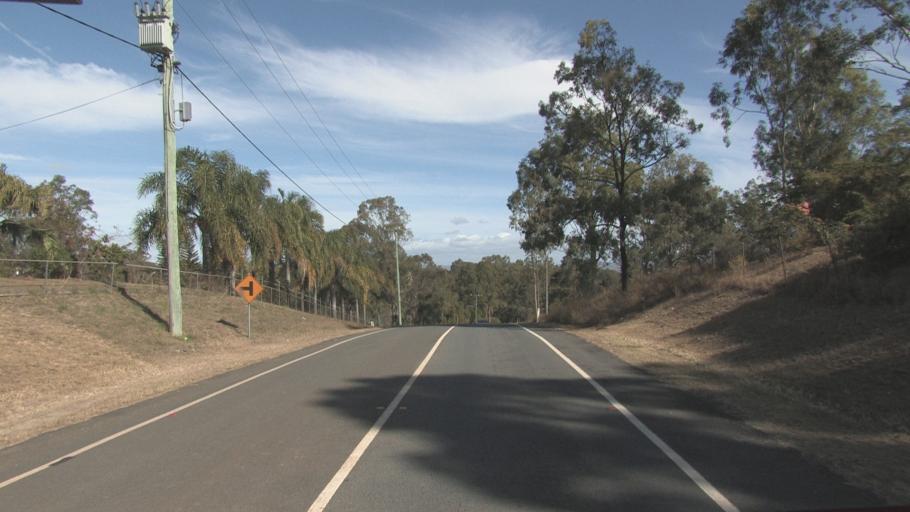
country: AU
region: Queensland
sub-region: Logan
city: Cedar Vale
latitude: -27.8798
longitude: 152.9915
